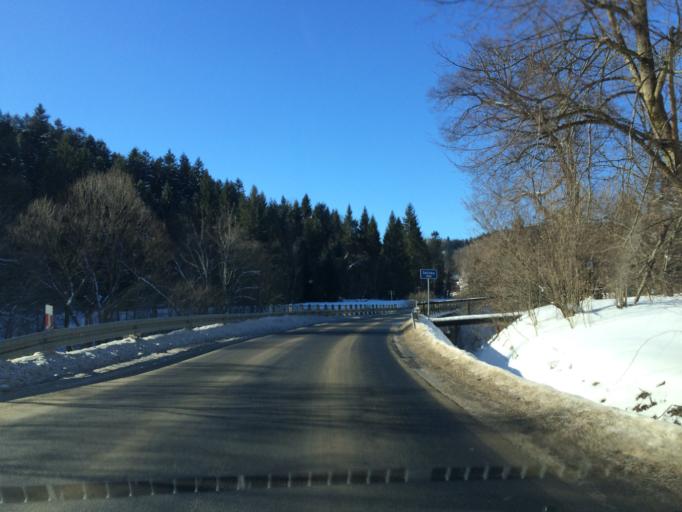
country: PL
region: Subcarpathian Voivodeship
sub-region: Powiat leski
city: Cisna
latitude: 49.2214
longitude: 22.3418
